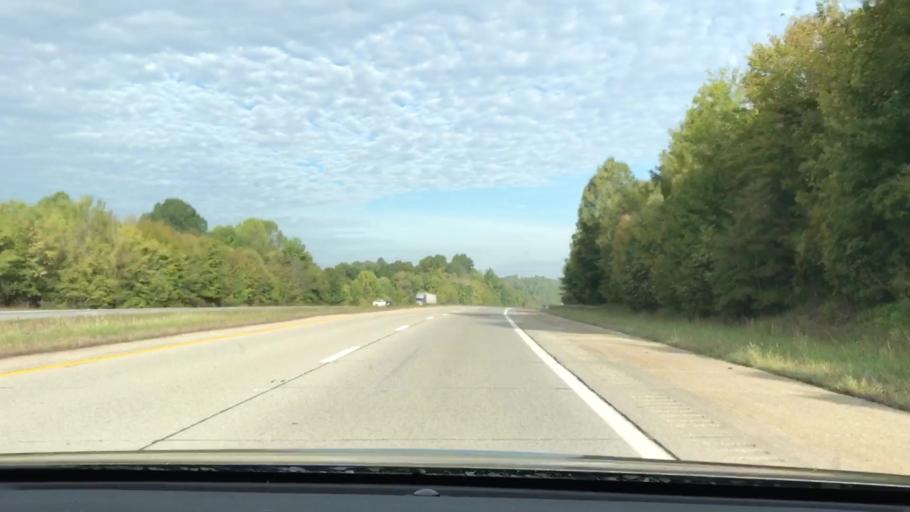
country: US
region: Kentucky
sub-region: Lyon County
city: Eddyville
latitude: 37.0297
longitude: -88.0003
